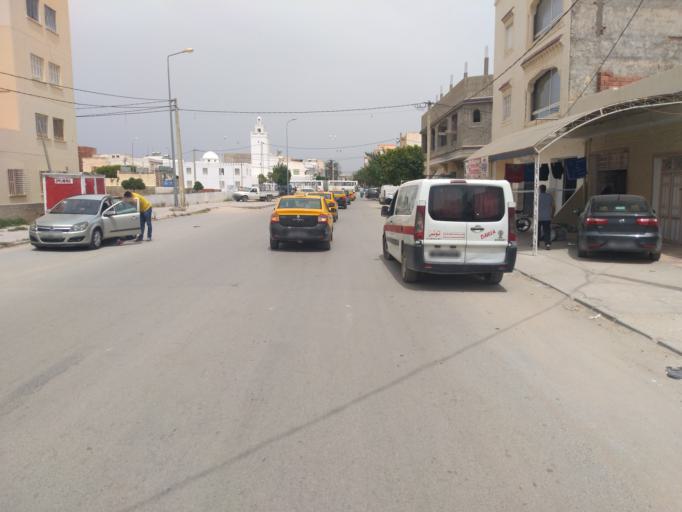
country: TN
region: Al Qayrawan
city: Kairouan
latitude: 35.6707
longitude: 10.0883
